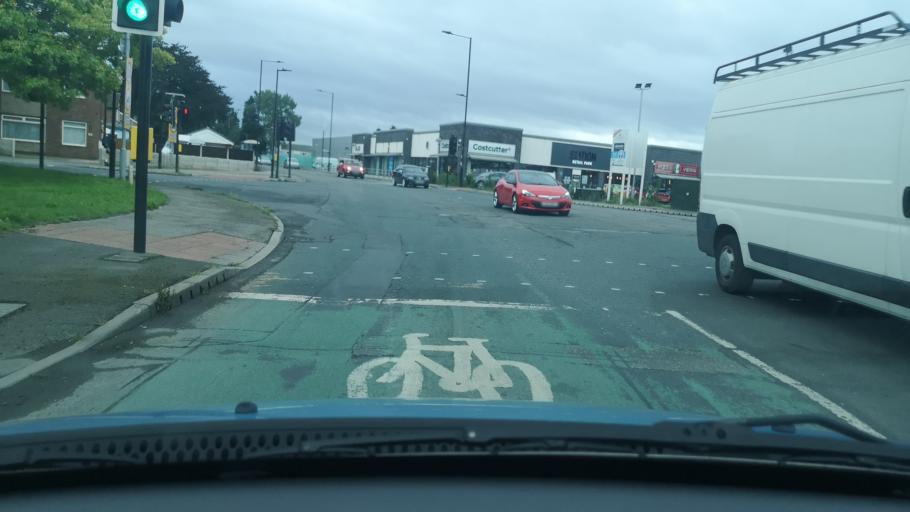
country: GB
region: England
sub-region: Doncaster
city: Kirk Sandall
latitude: 53.5641
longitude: -1.0725
